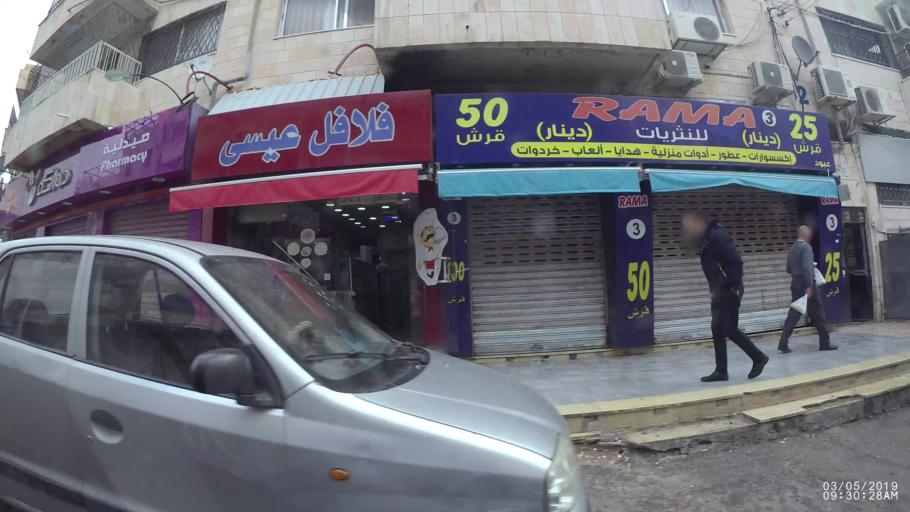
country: JO
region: Amman
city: Amman
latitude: 31.9742
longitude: 35.9261
